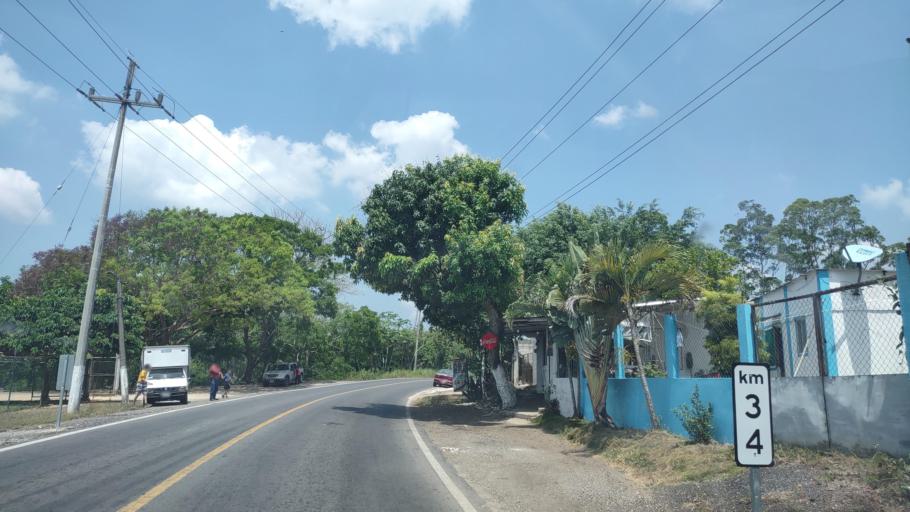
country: MX
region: Veracruz
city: Las Choapas
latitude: 17.9281
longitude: -94.1469
